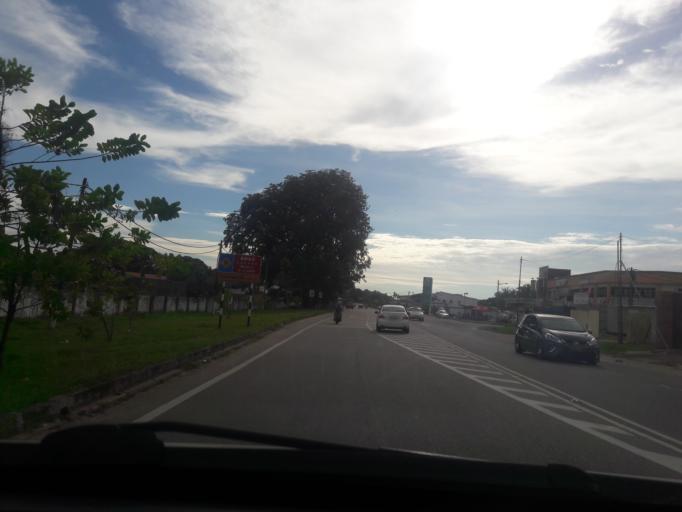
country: MY
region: Kedah
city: Sungai Petani
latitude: 5.6351
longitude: 100.5091
